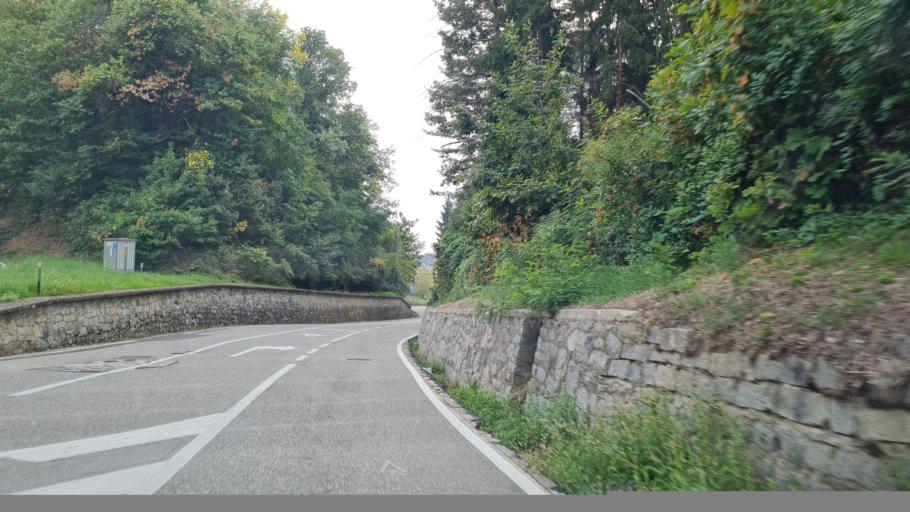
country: IT
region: Piedmont
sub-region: Provincia di Biella
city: Lessona
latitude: 45.5951
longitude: 8.1947
